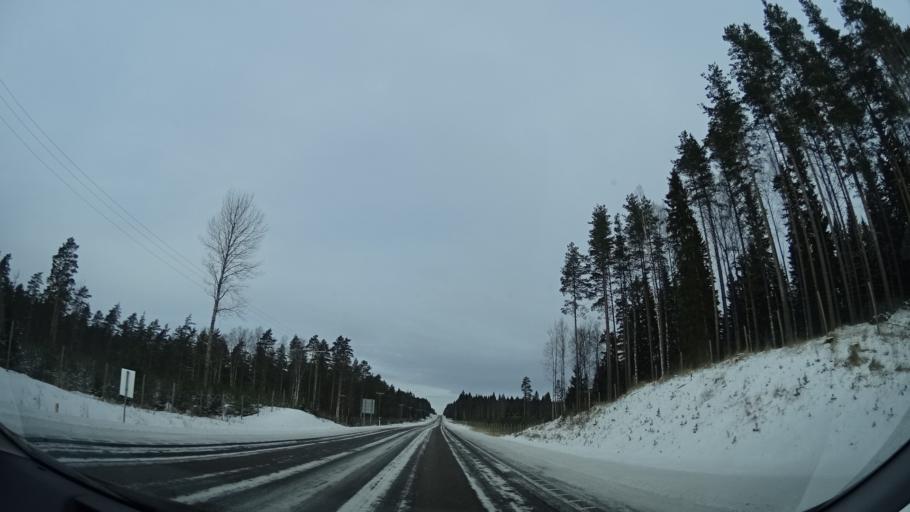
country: FI
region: Uusimaa
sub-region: Helsinki
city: Kaerkoelae
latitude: 60.6484
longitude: 23.8687
